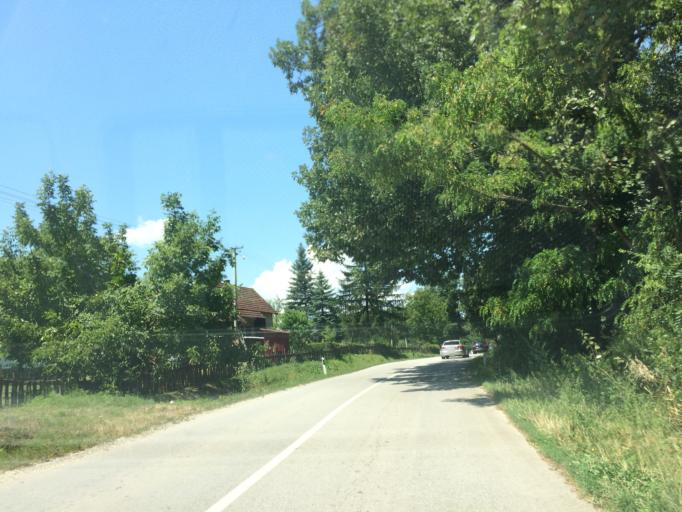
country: RS
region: Central Serbia
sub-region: Kolubarski Okrug
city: Ljig
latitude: 44.2353
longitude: 20.1908
